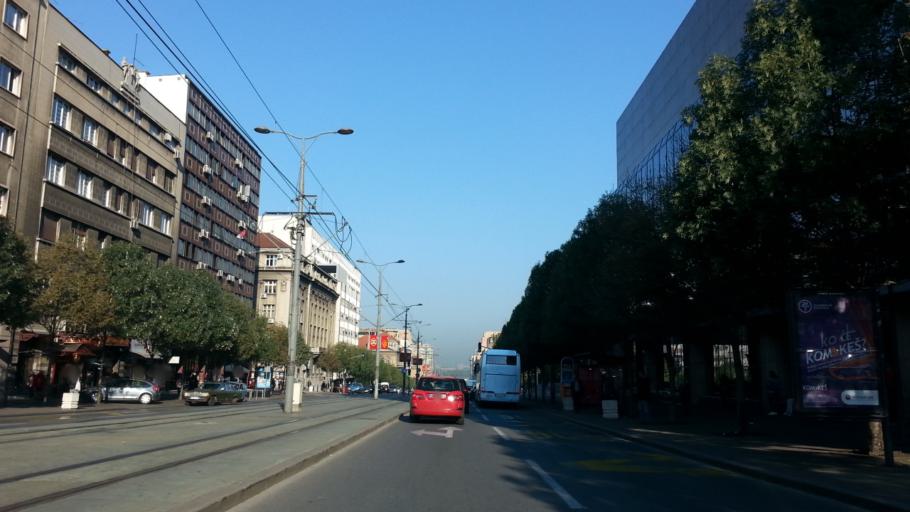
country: RS
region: Central Serbia
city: Belgrade
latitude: 44.8030
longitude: 20.4648
